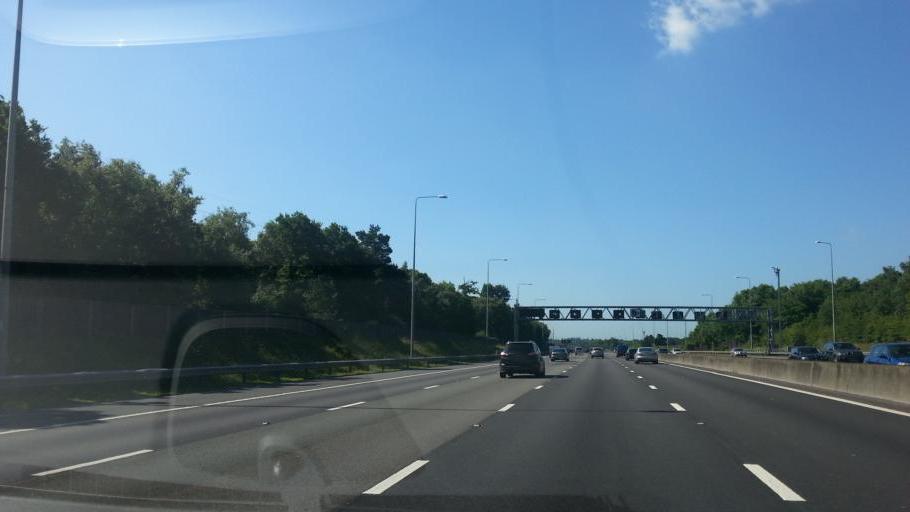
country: GB
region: England
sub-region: Buckinghamshire
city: Gerrards Cross
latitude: 51.5949
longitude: -0.5321
